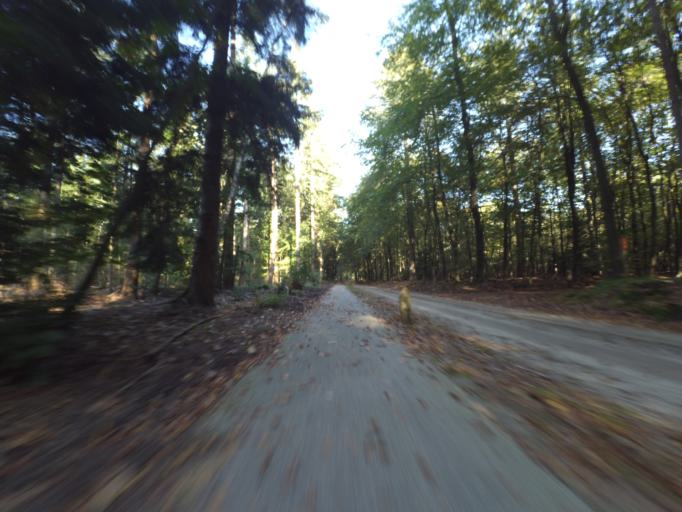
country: NL
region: Gelderland
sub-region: Gemeente Putten
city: Putten
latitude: 52.2531
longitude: 5.6402
